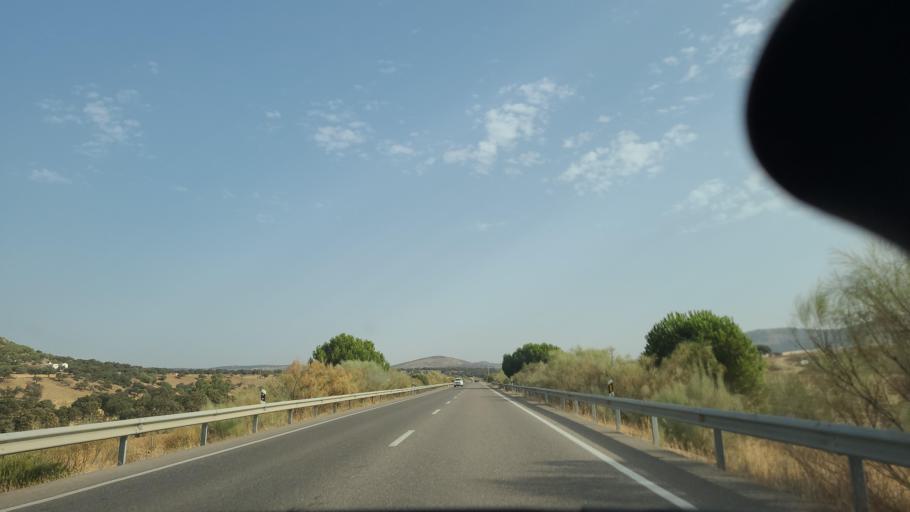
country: ES
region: Andalusia
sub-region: Province of Cordoba
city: Belmez
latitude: 38.2398
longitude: -5.1677
